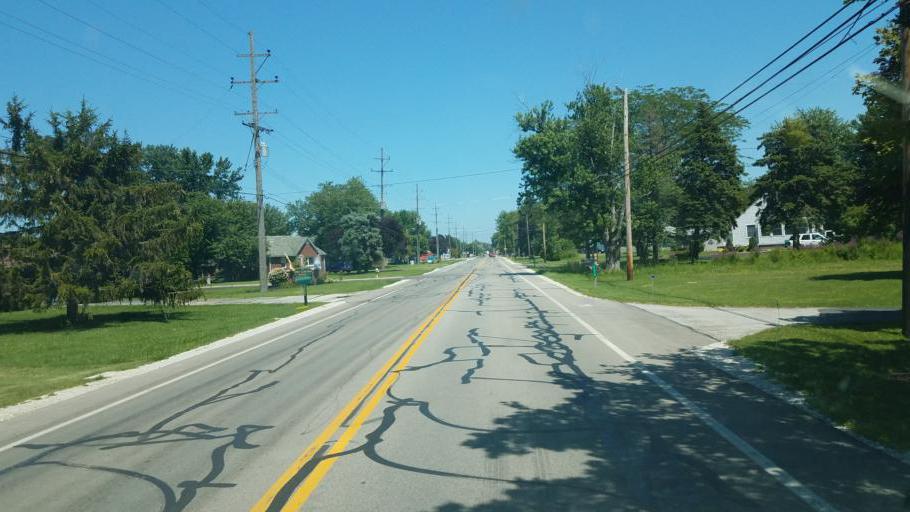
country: US
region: Ohio
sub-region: Ottawa County
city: Port Clinton
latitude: 41.5045
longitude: -82.9590
